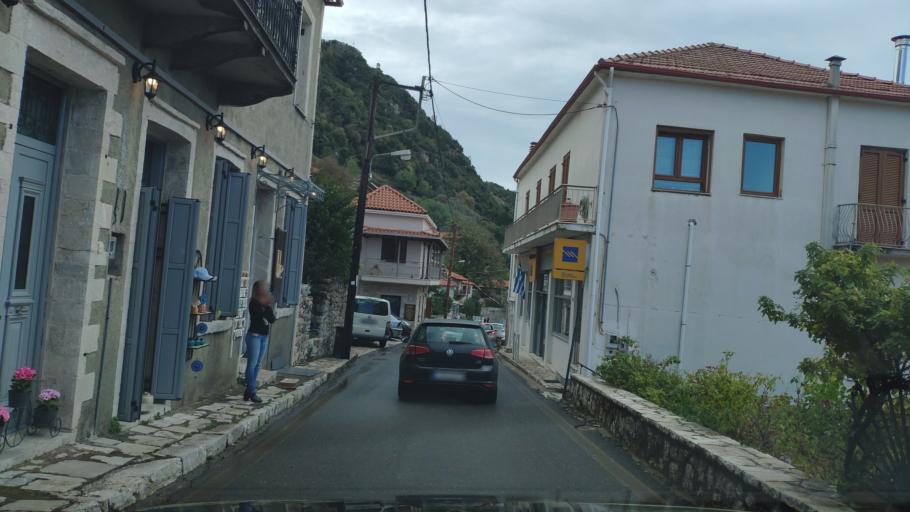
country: GR
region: Peloponnese
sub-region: Nomos Arkadias
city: Dimitsana
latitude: 37.5947
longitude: 22.0402
